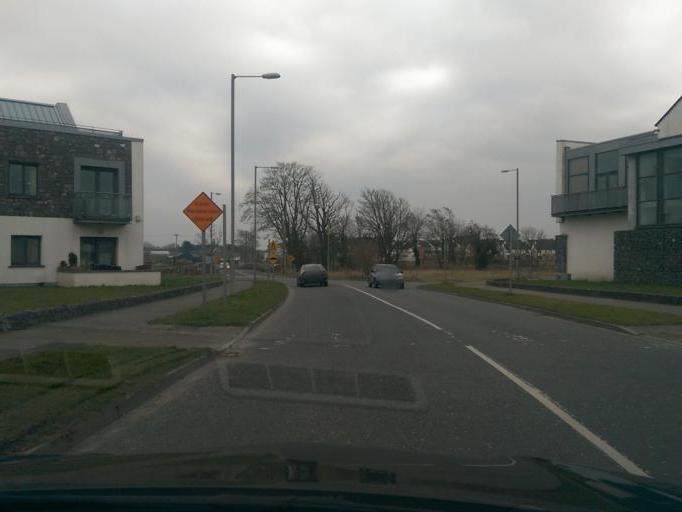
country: IE
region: Connaught
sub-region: County Galway
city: Athenry
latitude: 53.2942
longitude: -8.7488
